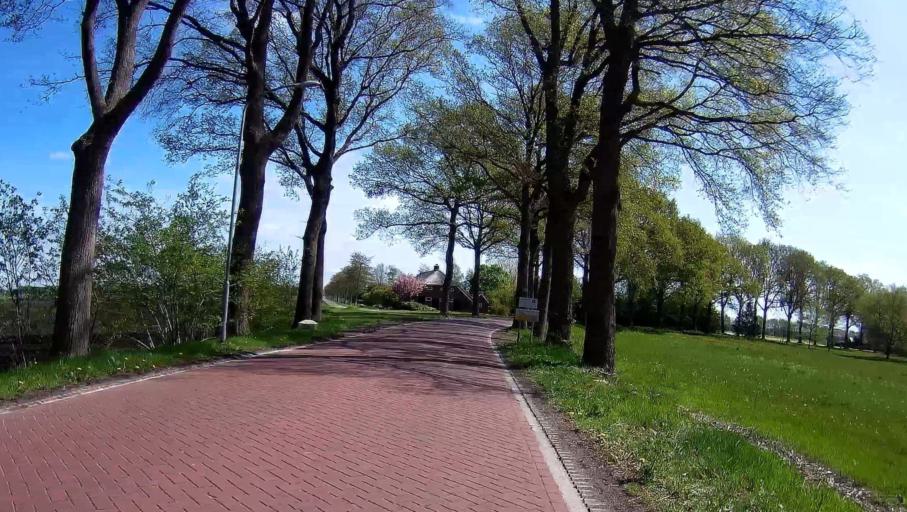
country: NL
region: Drenthe
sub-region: Gemeente Borger-Odoorn
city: Borger
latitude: 52.9707
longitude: 6.8130
